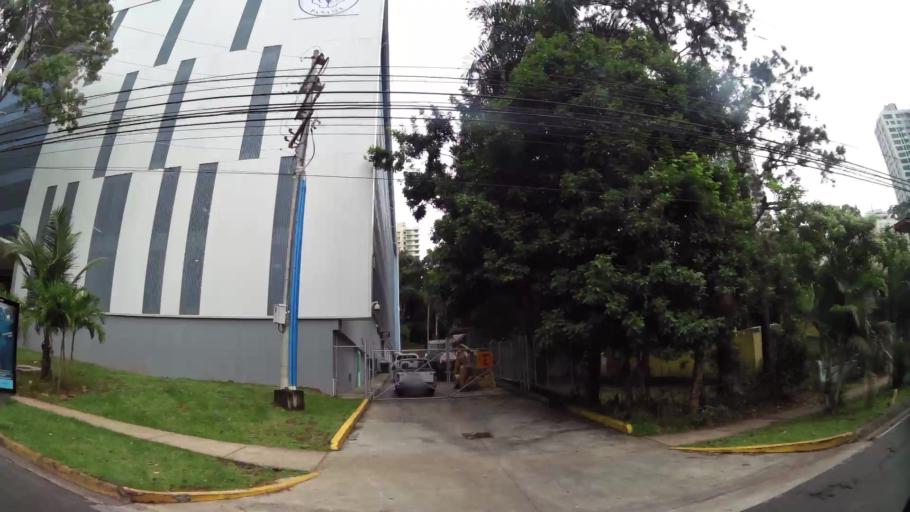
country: PA
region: Panama
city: Panama
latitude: 8.9817
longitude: -79.5327
